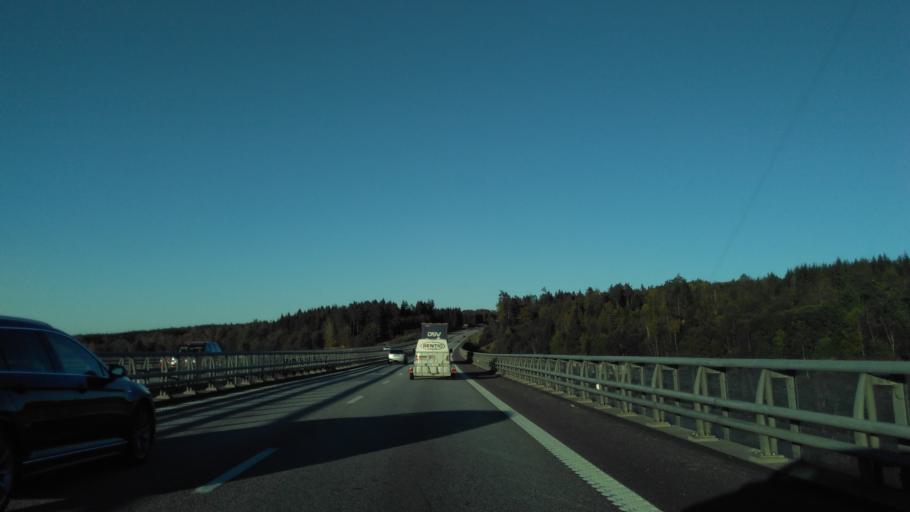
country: SE
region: Vaestra Goetaland
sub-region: Boras Kommun
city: Dalsjofors
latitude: 57.7853
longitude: 13.1246
